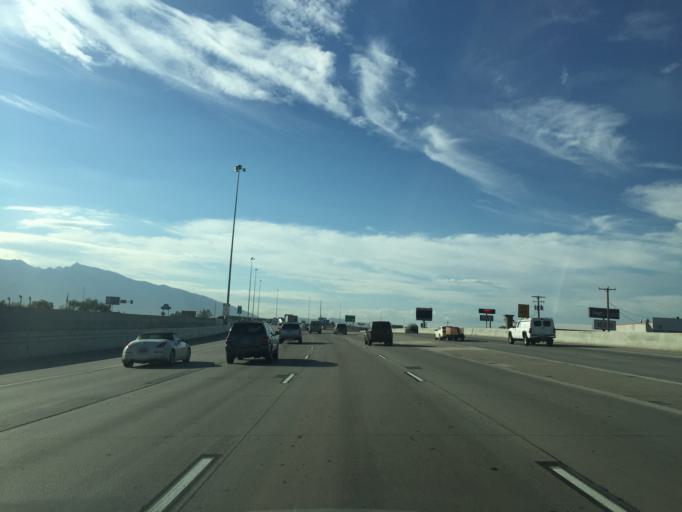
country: US
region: Utah
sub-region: Salt Lake County
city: Centerfield
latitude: 40.7042
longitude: -111.9037
